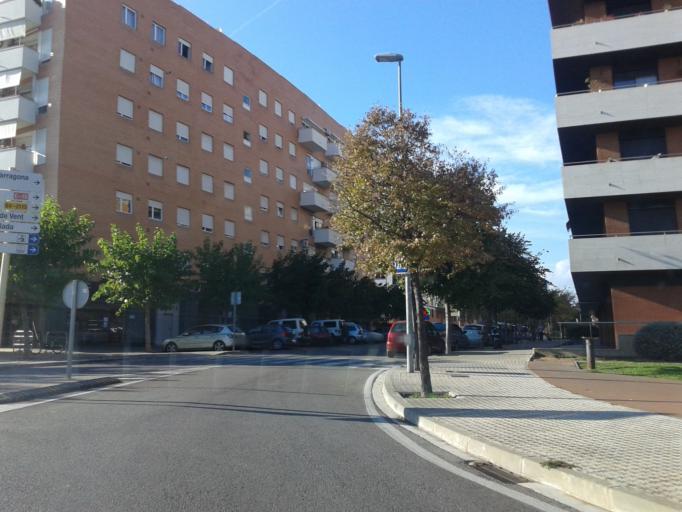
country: ES
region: Catalonia
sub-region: Provincia de Barcelona
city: Vilanova i la Geltru
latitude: 41.2182
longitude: 1.7133
